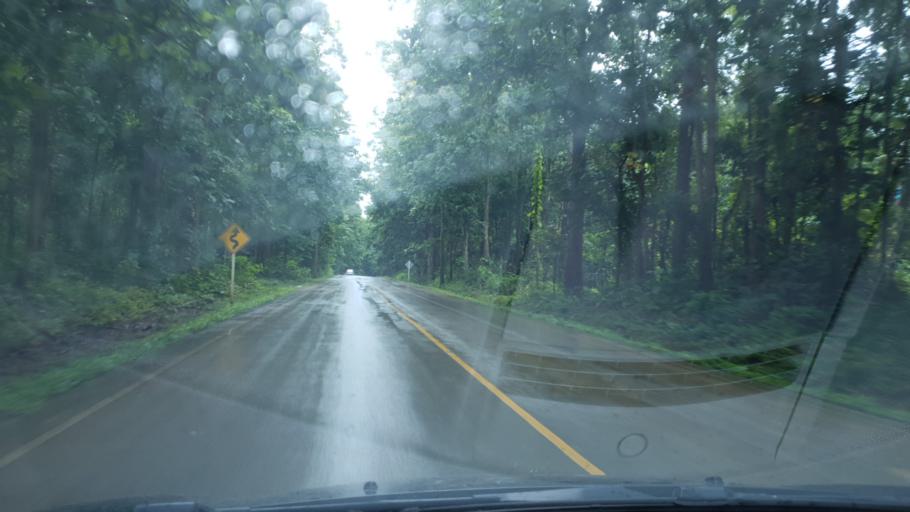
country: TH
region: Mae Hong Son
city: Pa Pae
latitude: 18.2500
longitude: 97.9433
